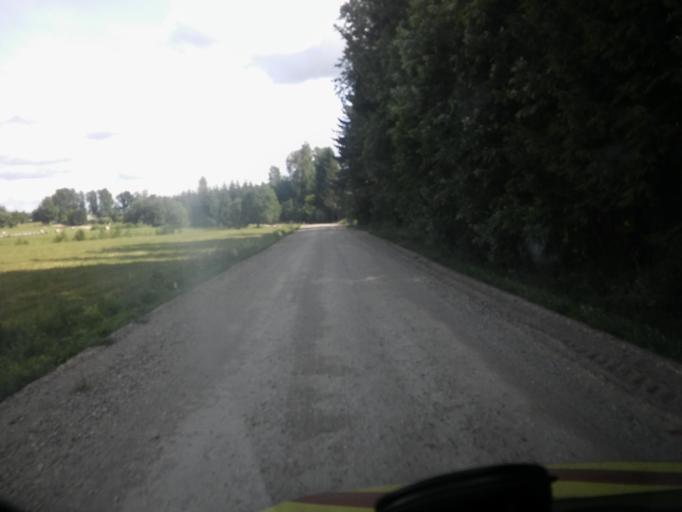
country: EE
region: Viljandimaa
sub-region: Karksi vald
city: Karksi-Nuia
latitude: 58.0592
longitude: 25.5413
